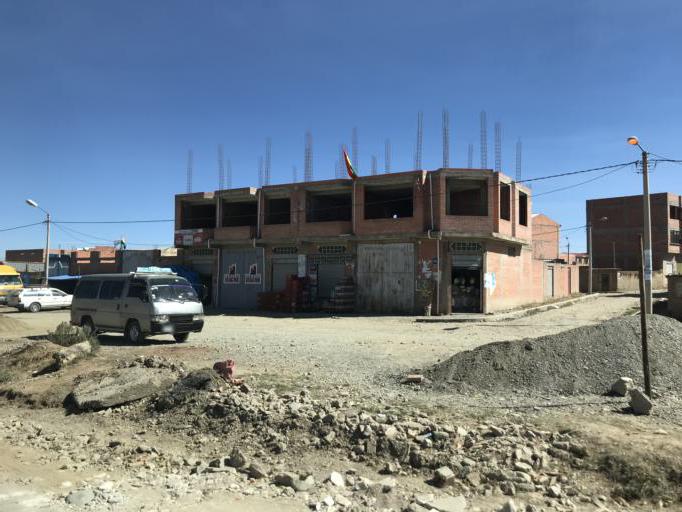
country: BO
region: La Paz
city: La Paz
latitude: -16.5017
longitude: -68.2414
